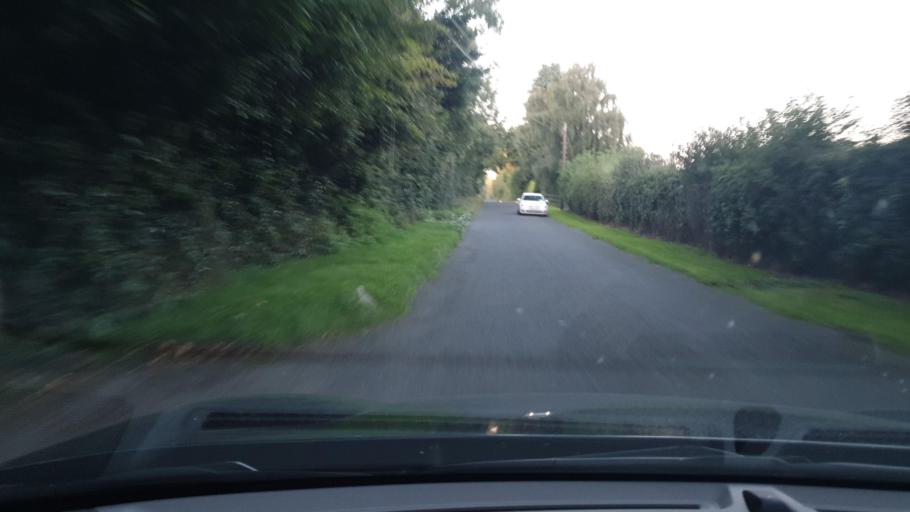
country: IE
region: Leinster
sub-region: Kildare
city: Prosperous
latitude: 53.3205
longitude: -6.8038
